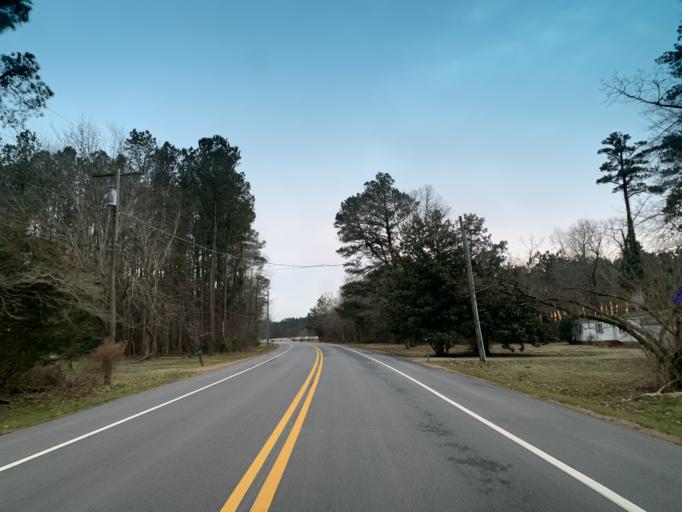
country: US
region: Maryland
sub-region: Worcester County
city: Pocomoke City
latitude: 38.0799
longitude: -75.5436
